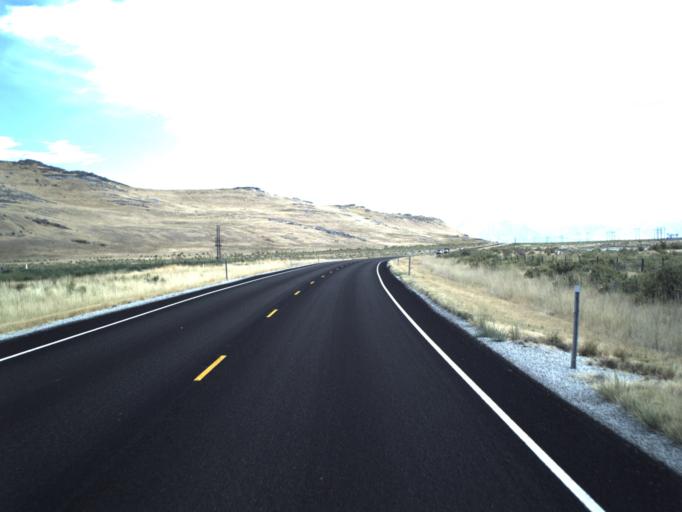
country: US
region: Utah
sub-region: Box Elder County
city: Tremonton
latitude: 41.6259
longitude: -112.3958
